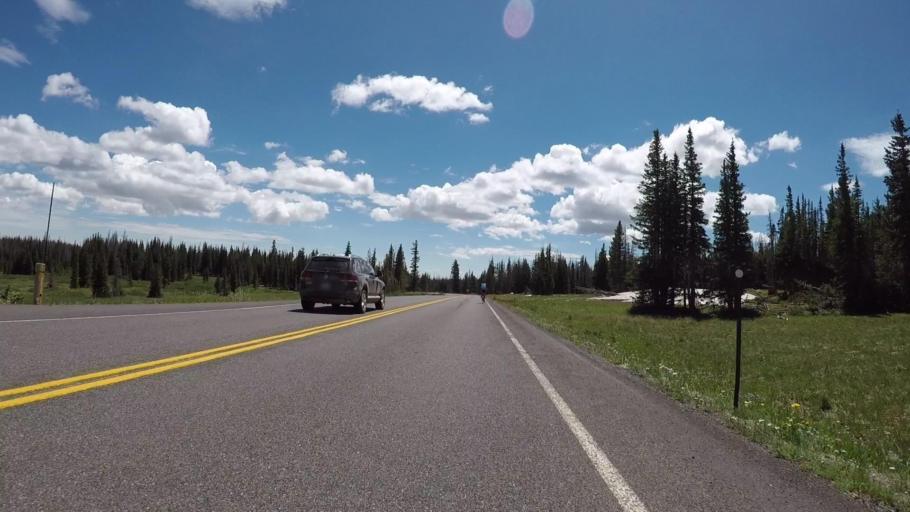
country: US
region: Wyoming
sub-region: Carbon County
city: Saratoga
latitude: 41.3512
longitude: -106.2592
